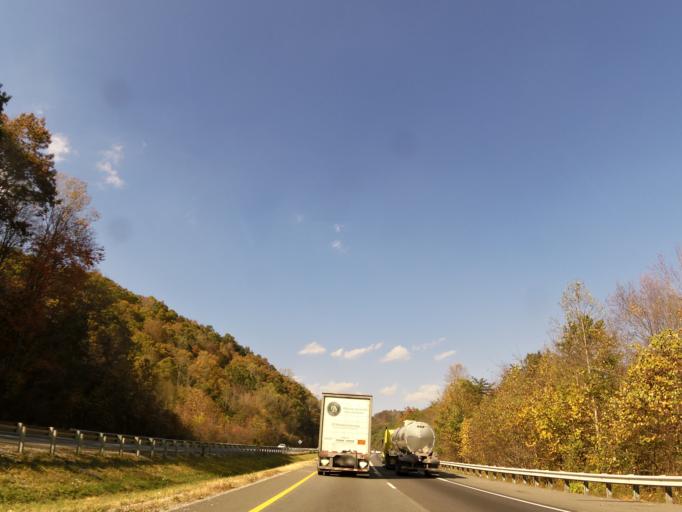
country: US
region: Tennessee
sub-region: Campbell County
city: Caryville
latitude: 36.3285
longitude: -84.2269
